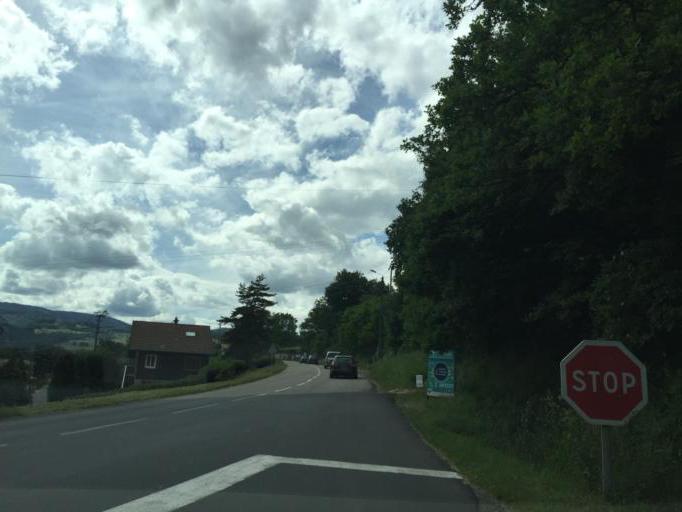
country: FR
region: Auvergne
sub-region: Departement du Puy-de-Dome
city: Ambert
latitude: 45.5437
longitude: 3.7574
